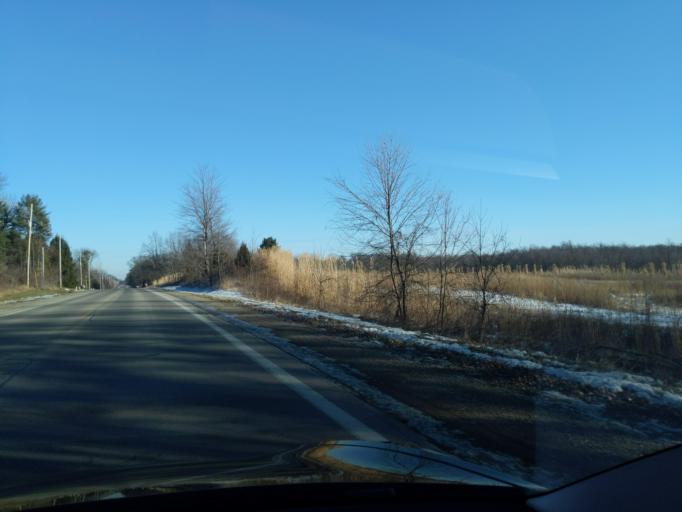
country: US
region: Michigan
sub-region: Ingham County
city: Stockbridge
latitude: 42.3936
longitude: -84.2897
